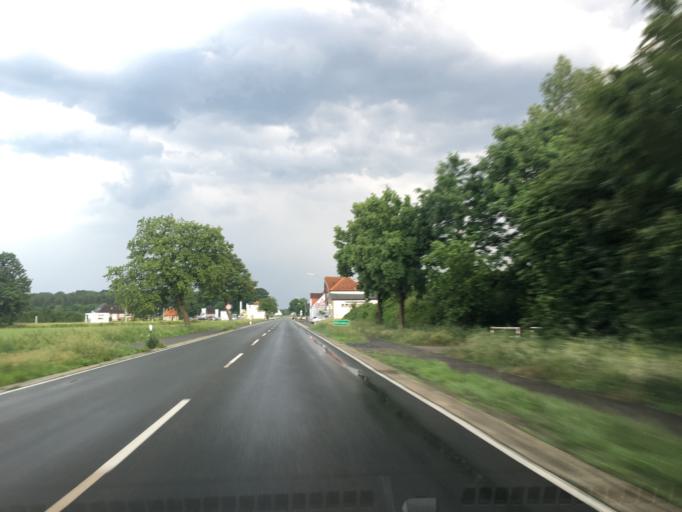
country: DE
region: North Rhine-Westphalia
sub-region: Regierungsbezirk Munster
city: Laer
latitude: 52.1072
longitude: 7.4036
